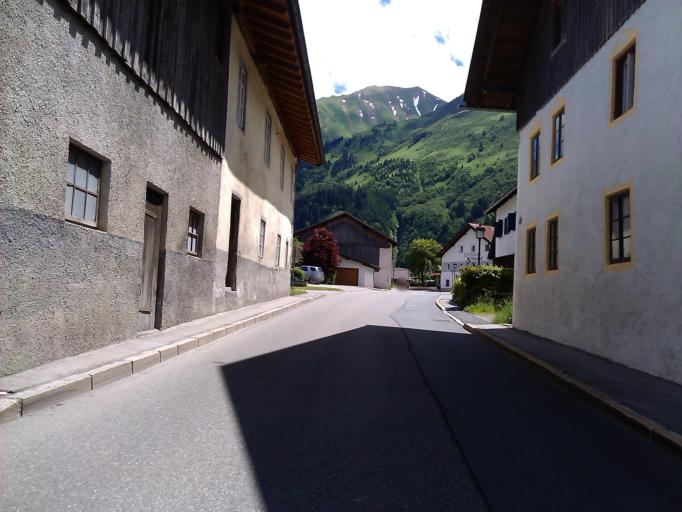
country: AT
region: Tyrol
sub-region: Politischer Bezirk Reutte
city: Bichlbach
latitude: 47.4211
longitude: 10.7867
